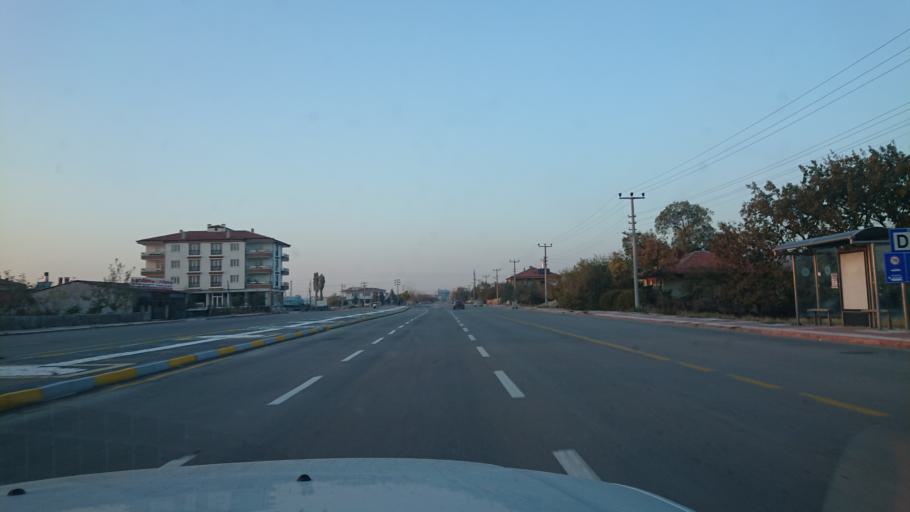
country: TR
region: Aksaray
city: Aksaray
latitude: 38.3424
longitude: 34.0462
